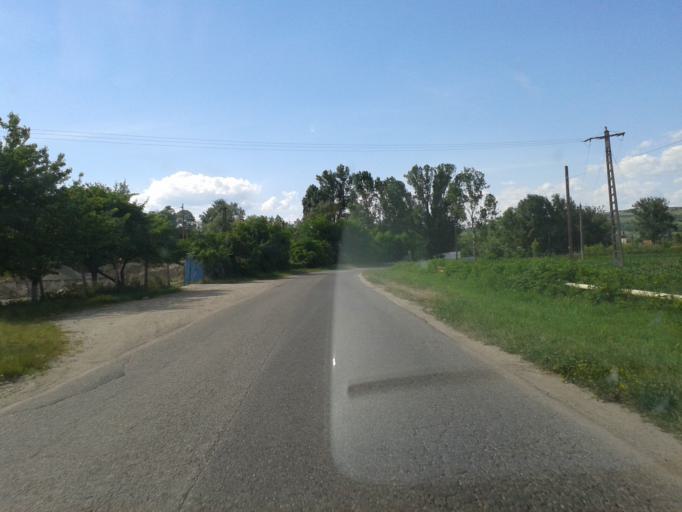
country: RO
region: Hunedoara
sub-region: Comuna Geoagiu
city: Geoagiu
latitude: 45.8940
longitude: 23.2270
